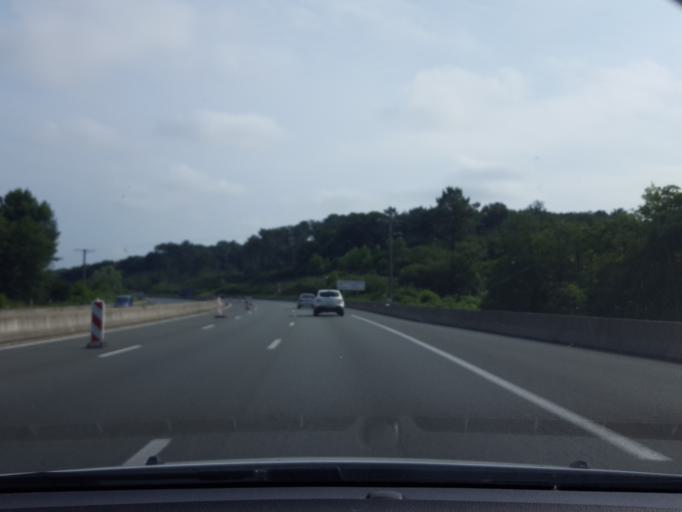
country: FR
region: Aquitaine
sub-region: Departement des Landes
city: Tarnos
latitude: 43.5319
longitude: -1.4320
